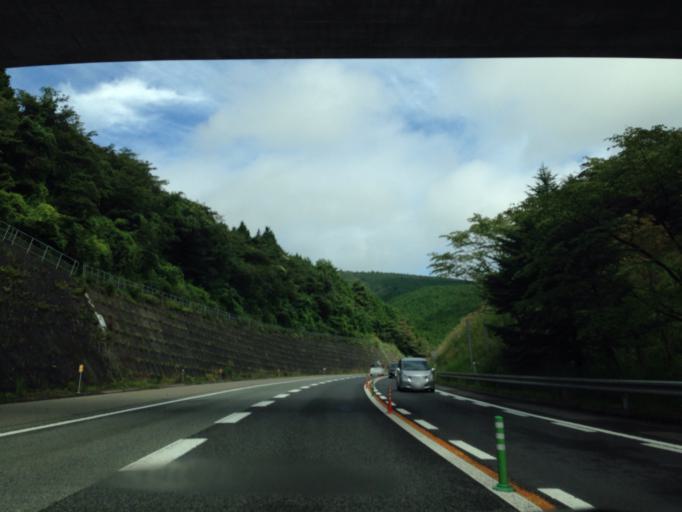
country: JP
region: Shizuoka
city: Gotemba
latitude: 35.3637
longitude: 138.8492
